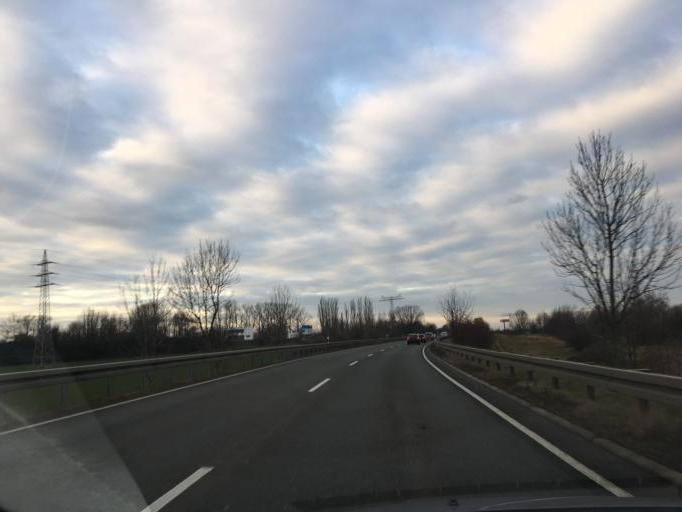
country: DE
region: Thuringia
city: Altenburg
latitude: 51.0056
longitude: 12.4615
